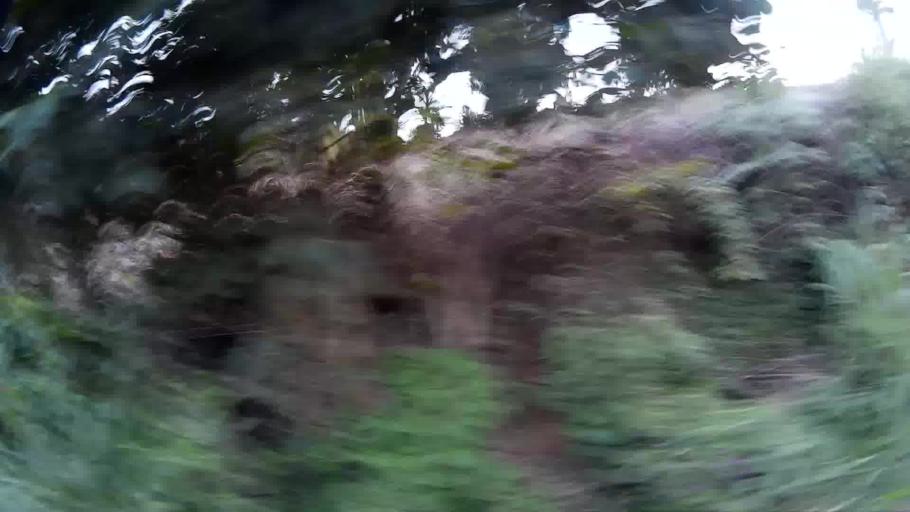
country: CO
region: Valle del Cauca
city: Ulloa
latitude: 4.7314
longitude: -75.7198
